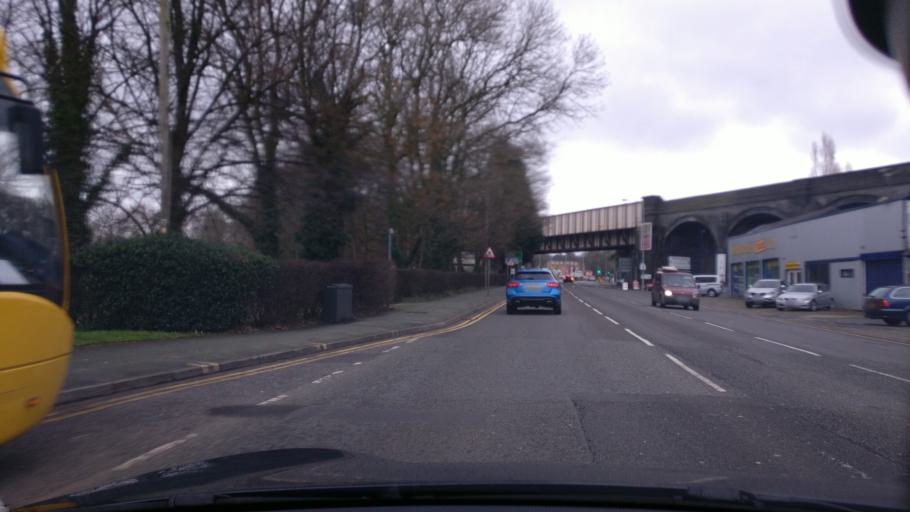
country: GB
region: England
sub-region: Borough of Stockport
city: Hazel Grove
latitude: 53.3752
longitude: -2.1126
